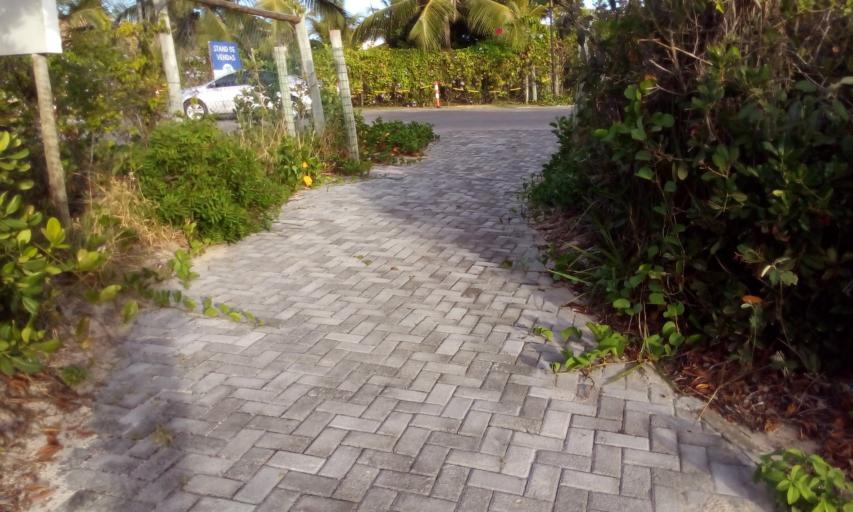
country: BR
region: Bahia
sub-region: Mata De Sao Joao
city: Mata de Sao Joao
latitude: -12.5703
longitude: -38.0018
